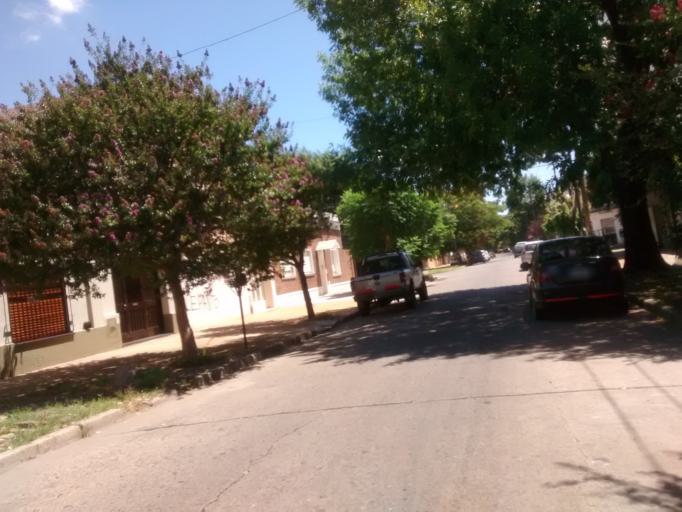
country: AR
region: Buenos Aires
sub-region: Partido de La Plata
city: La Plata
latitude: -34.9270
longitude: -57.9310
